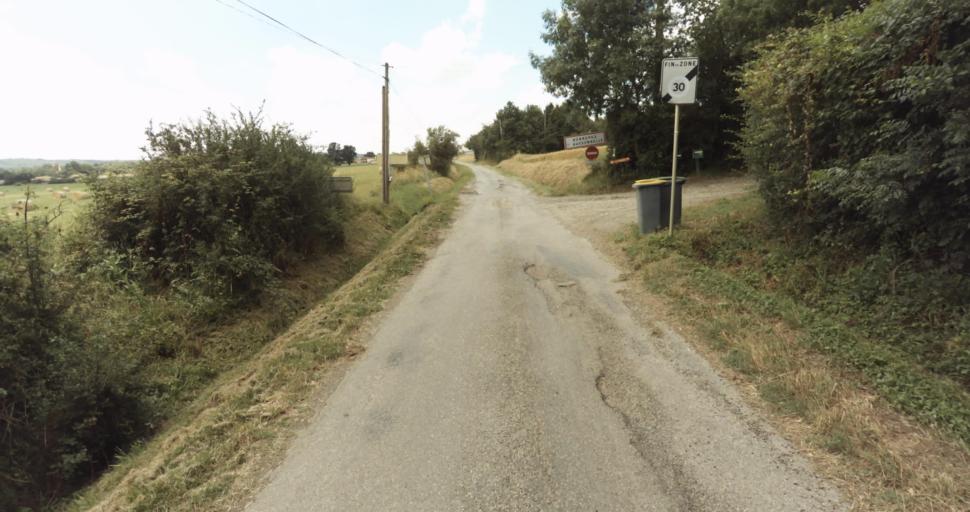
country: FR
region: Midi-Pyrenees
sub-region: Departement de la Haute-Garonne
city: Fontenilles
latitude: 43.5518
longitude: 1.1577
